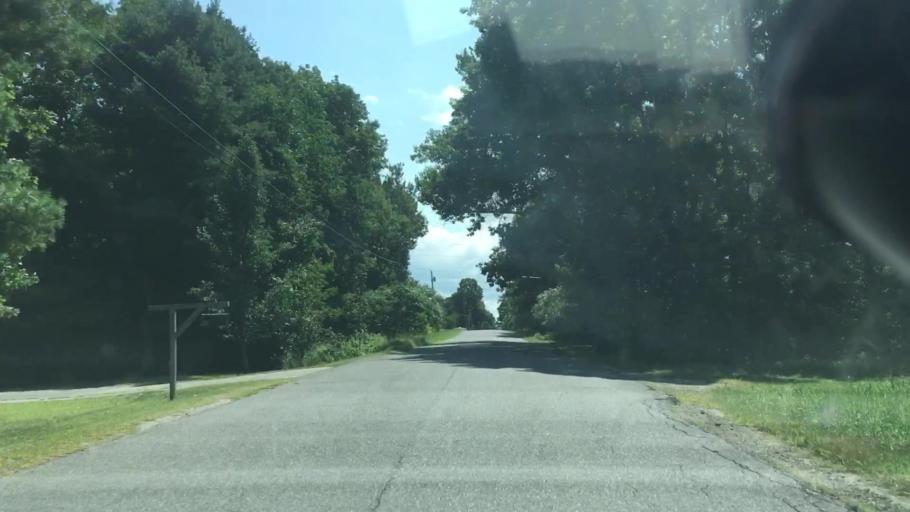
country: US
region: Maine
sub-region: Somerset County
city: Skowhegan
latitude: 44.6863
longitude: -69.6909
